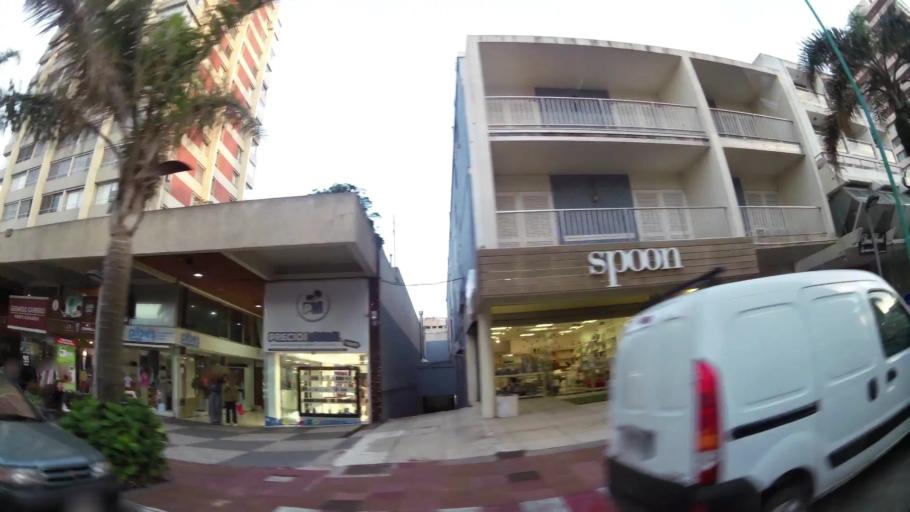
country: UY
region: Maldonado
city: Punta del Este
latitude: -34.9606
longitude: -54.9416
